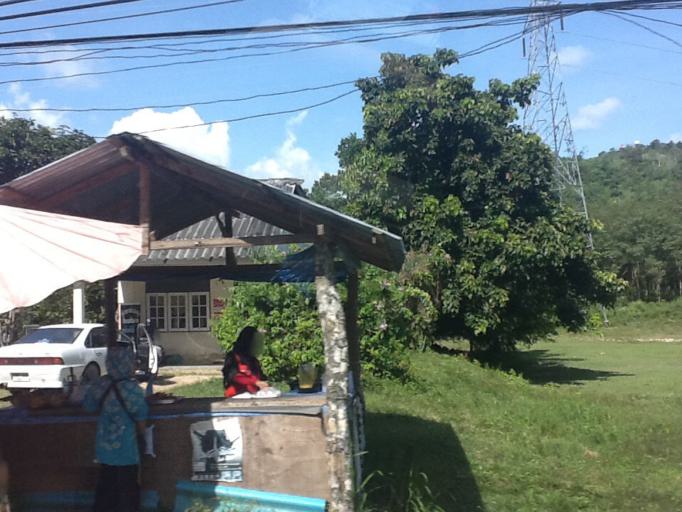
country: TH
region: Phuket
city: Thalang
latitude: 8.1242
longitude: 98.3216
